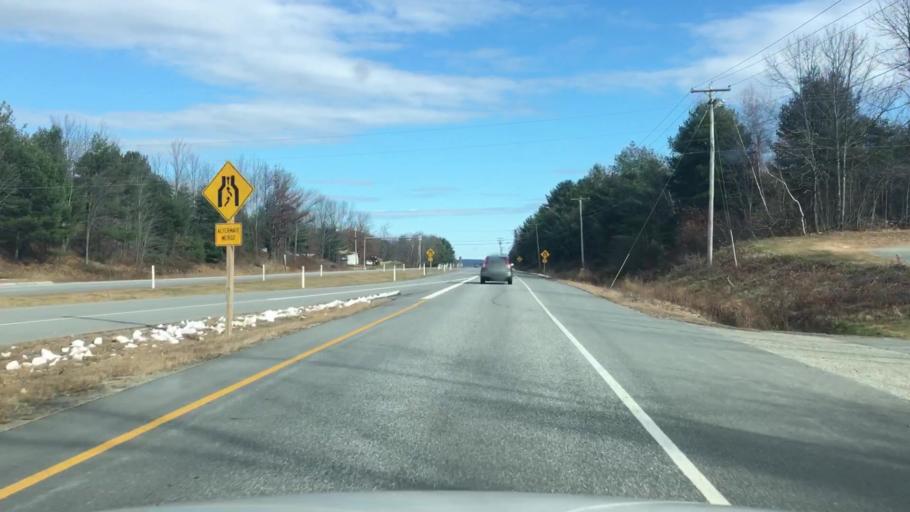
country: US
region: Maine
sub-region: Kennebec County
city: Winthrop
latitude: 44.3068
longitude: -69.9562
